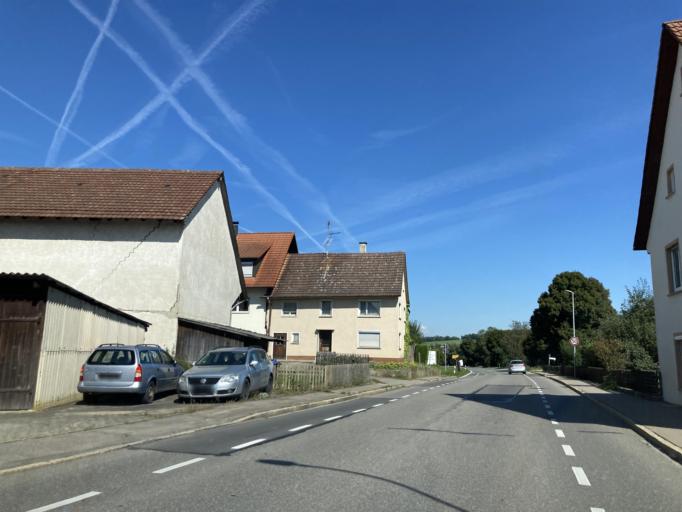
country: DE
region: Baden-Wuerttemberg
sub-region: Tuebingen Region
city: Unlingen
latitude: 48.1440
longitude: 9.5324
